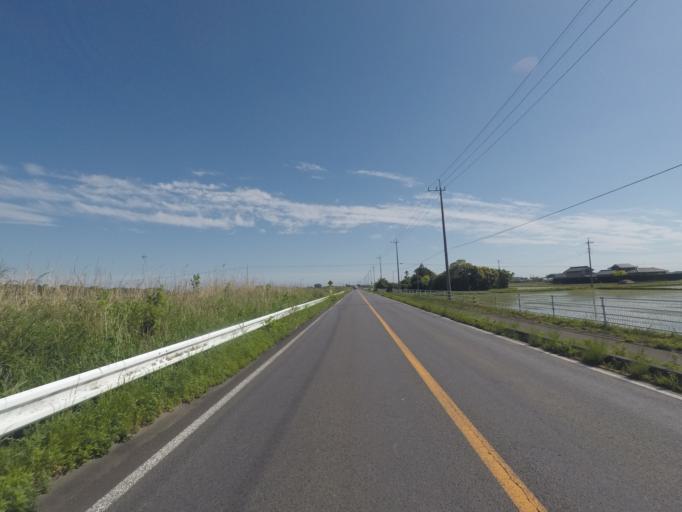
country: JP
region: Ibaraki
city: Inashiki
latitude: 36.0816
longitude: 140.4213
